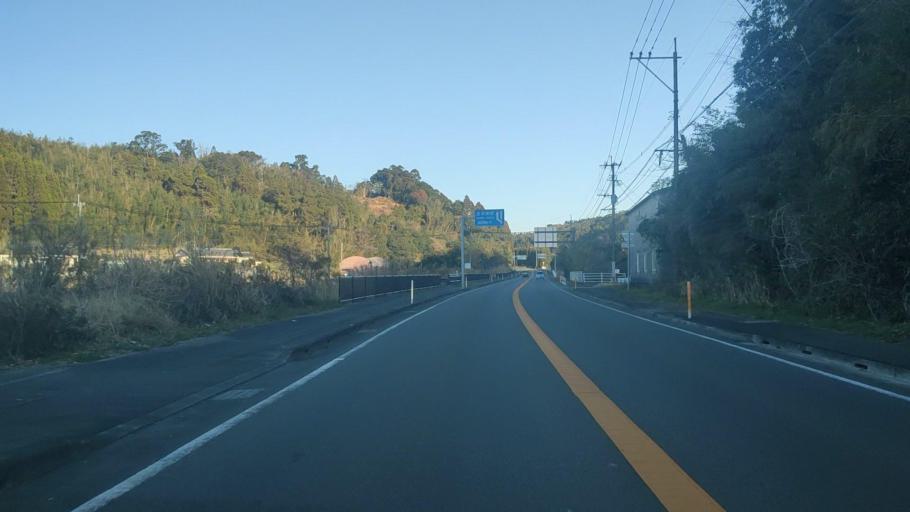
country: JP
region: Miyazaki
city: Takanabe
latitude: 32.1469
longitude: 131.5255
